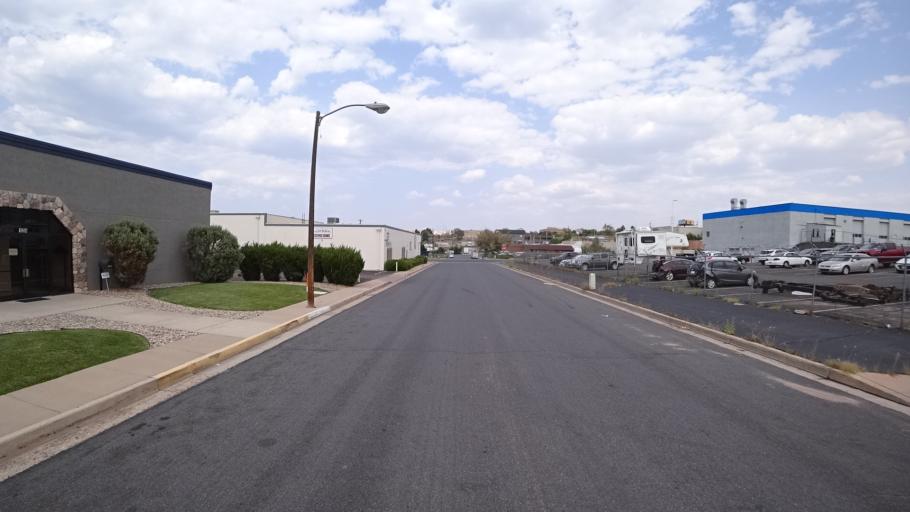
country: US
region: Colorado
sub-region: El Paso County
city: Colorado Springs
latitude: 38.8366
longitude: -104.7602
